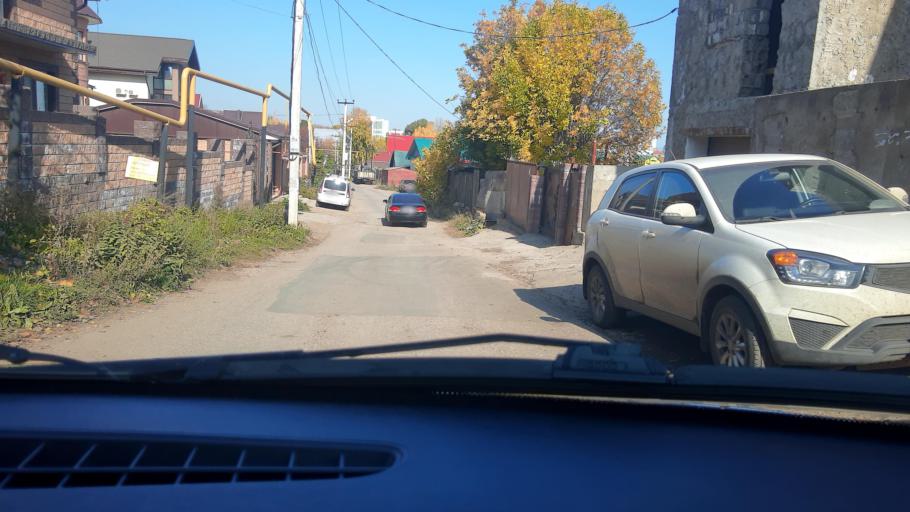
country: RU
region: Bashkortostan
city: Ufa
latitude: 54.7568
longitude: 56.0427
